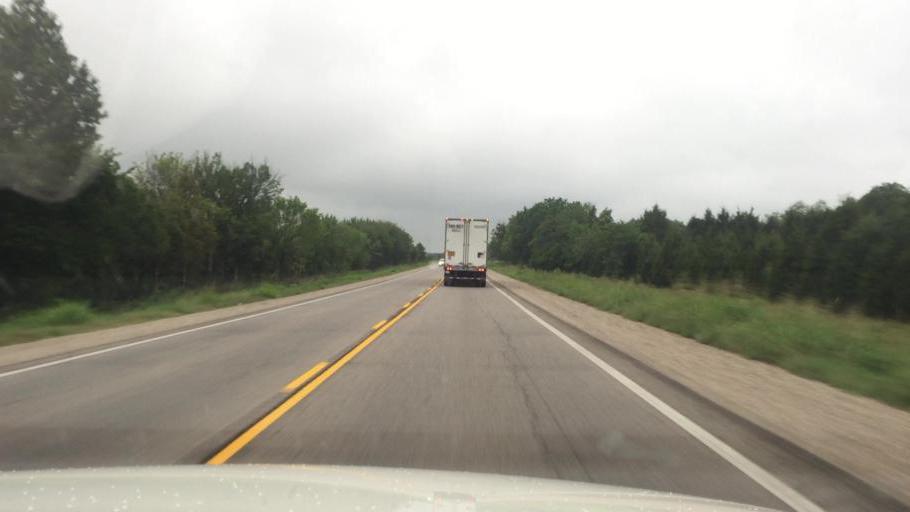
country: US
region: Kansas
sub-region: Montgomery County
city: Coffeyville
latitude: 37.1447
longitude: -95.5769
